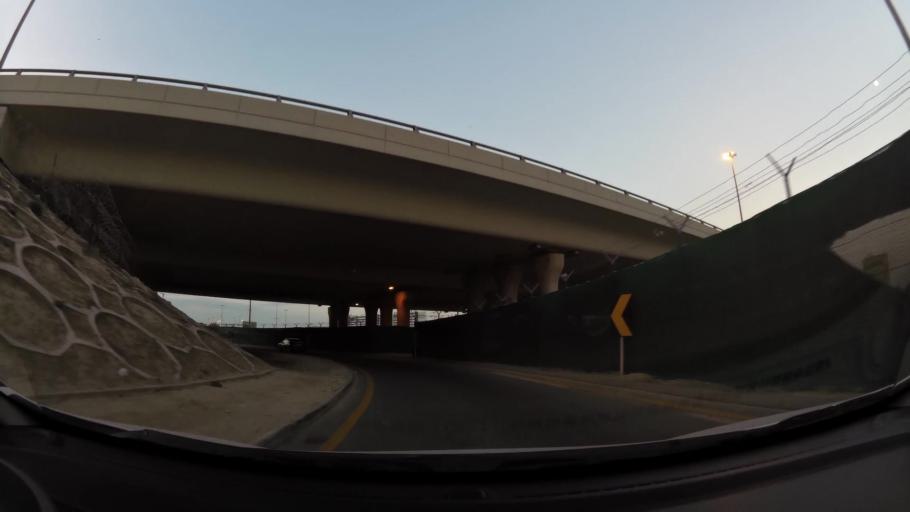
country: BH
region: Manama
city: Jidd Hafs
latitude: 26.2316
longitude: 50.5608
